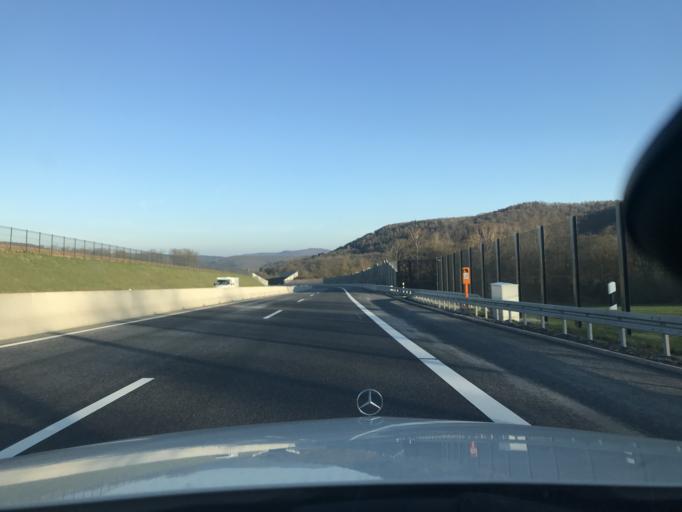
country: DE
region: Hesse
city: Waldkappel
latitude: 51.1541
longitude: 9.8924
